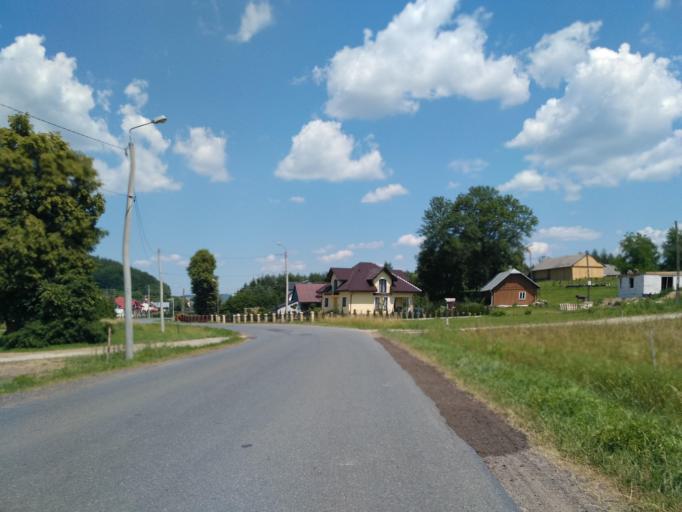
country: PL
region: Subcarpathian Voivodeship
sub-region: Powiat sanocki
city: Niebieszczany
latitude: 49.5439
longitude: 22.1344
